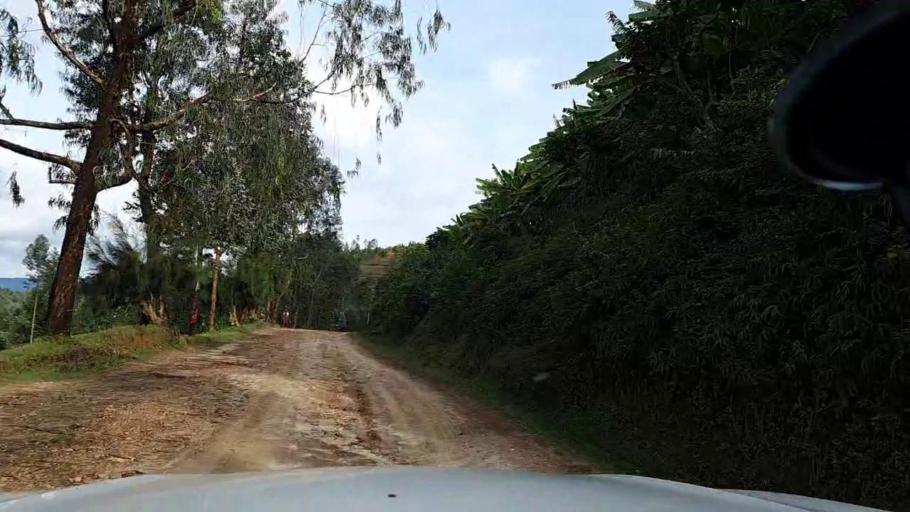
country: RW
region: Western Province
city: Kibuye
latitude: -2.1623
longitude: 29.5484
